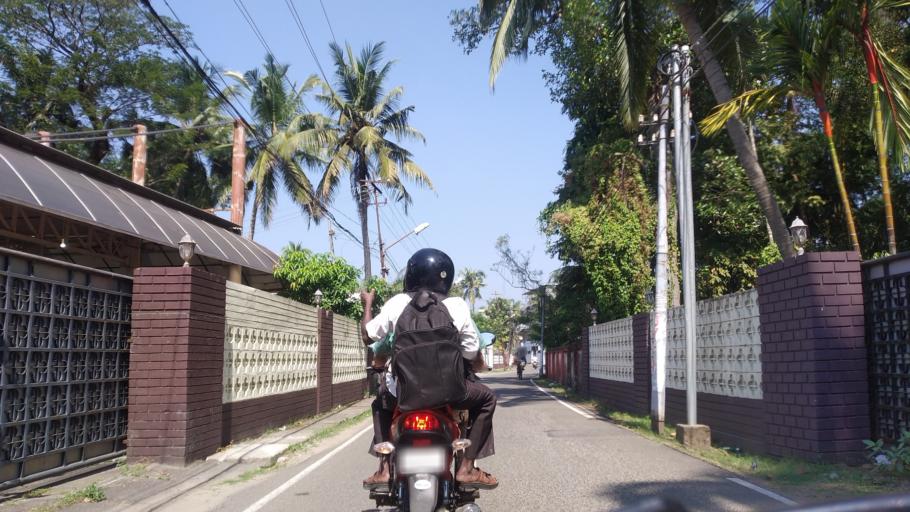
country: IN
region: Kerala
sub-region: Ernakulam
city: Cochin
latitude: 9.9403
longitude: 76.2484
